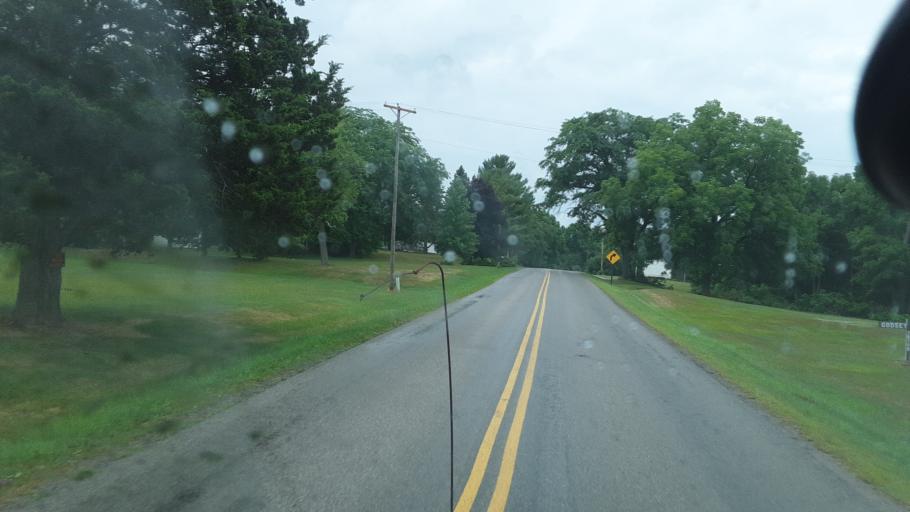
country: US
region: Indiana
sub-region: Steuben County
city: Hamilton
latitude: 41.6371
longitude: -84.7900
